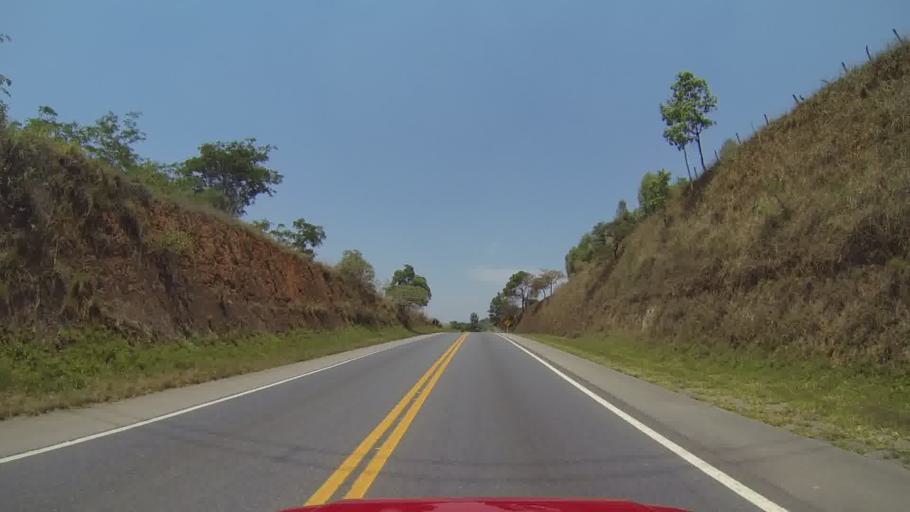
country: BR
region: Minas Gerais
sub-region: Itapecerica
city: Itapecerica
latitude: -20.3144
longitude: -45.2216
